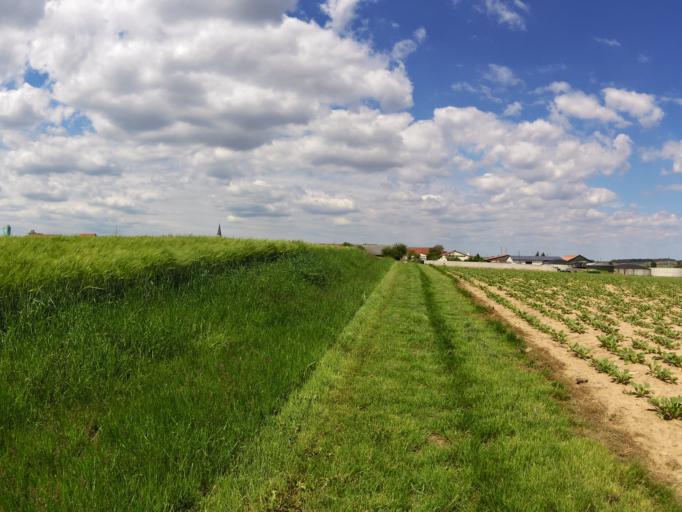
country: DE
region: Bavaria
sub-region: Regierungsbezirk Unterfranken
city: Biebelried
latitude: 49.7399
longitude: 10.0675
